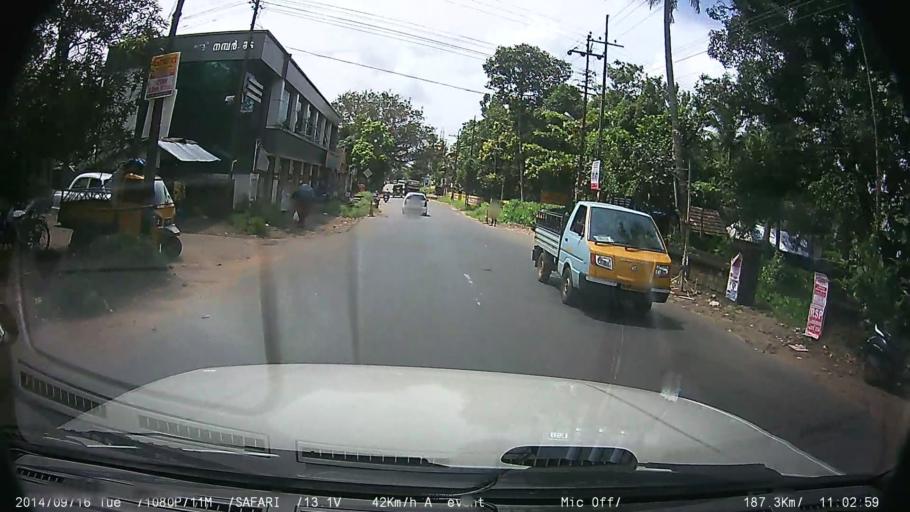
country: IN
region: Kerala
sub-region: Kottayam
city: Kottayam
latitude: 9.5474
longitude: 76.5140
